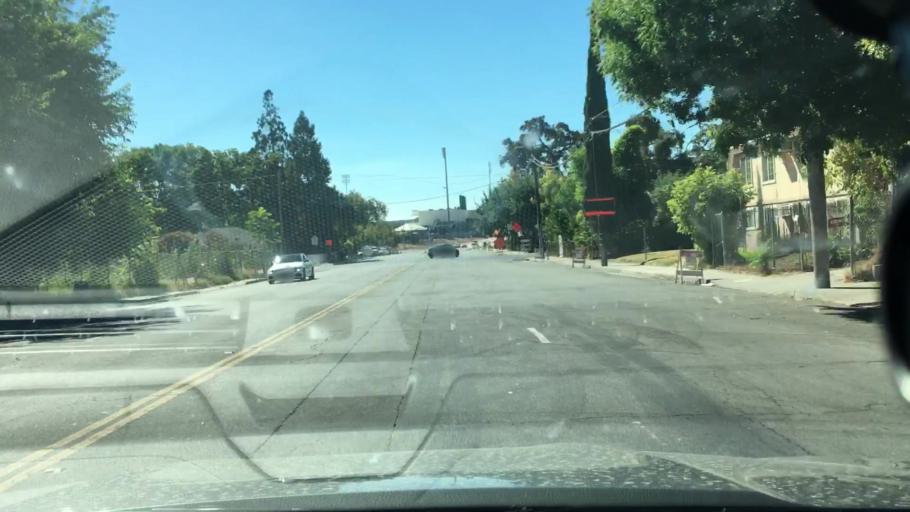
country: US
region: California
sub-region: Yolo County
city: West Sacramento
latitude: 38.5847
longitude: -121.5136
